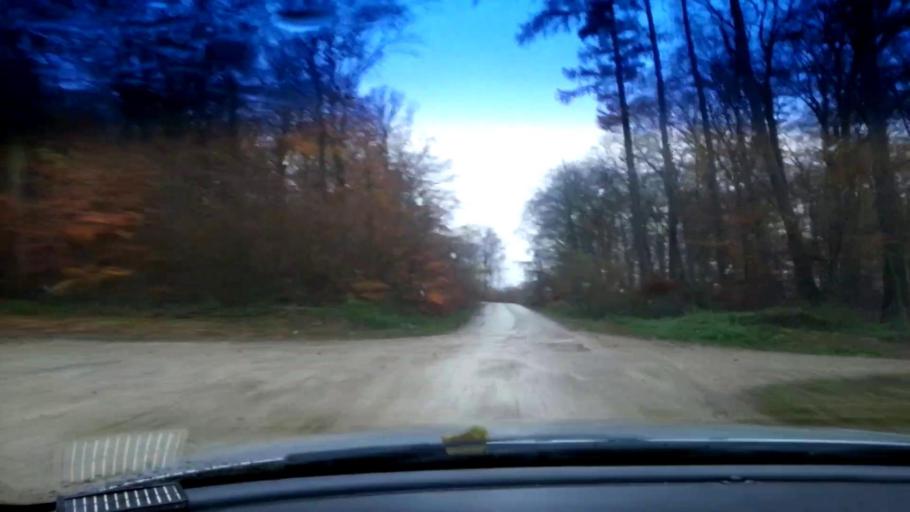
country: DE
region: Bavaria
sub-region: Upper Franconia
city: Schesslitz
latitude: 49.9437
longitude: 11.0257
